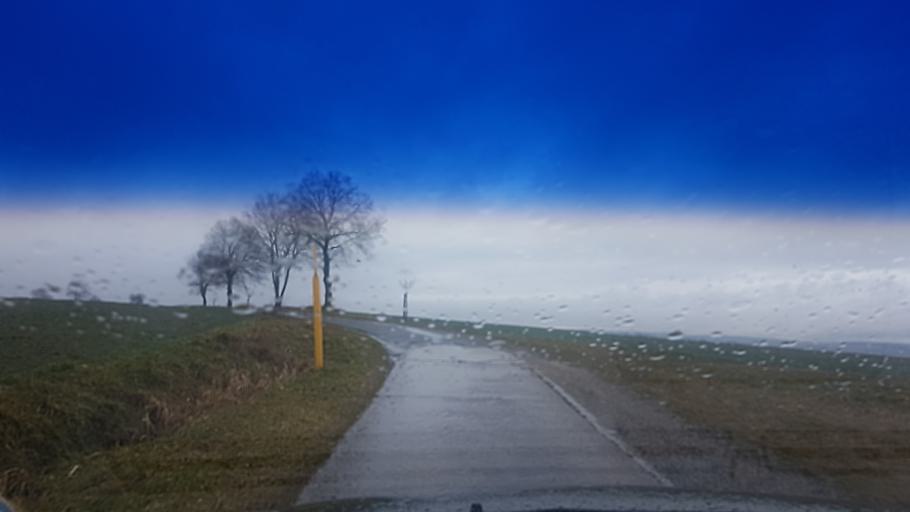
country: DE
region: Bavaria
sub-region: Upper Franconia
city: Burgebrach
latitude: 49.8082
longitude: 10.7673
